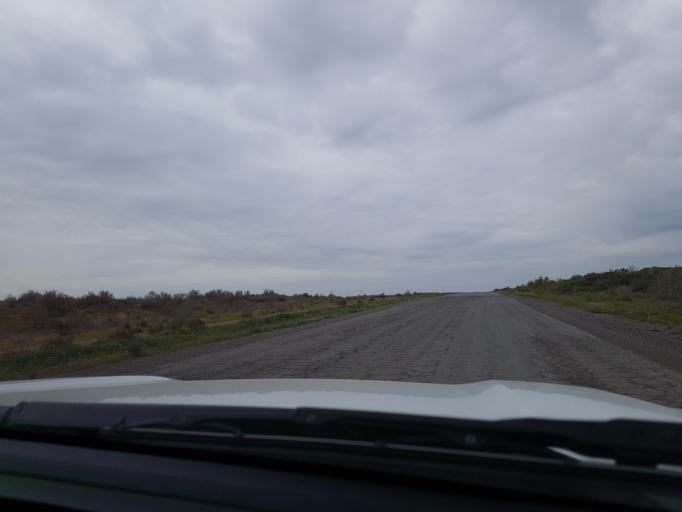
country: TM
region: Mary
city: Bayramaly
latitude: 37.9130
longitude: 62.6214
